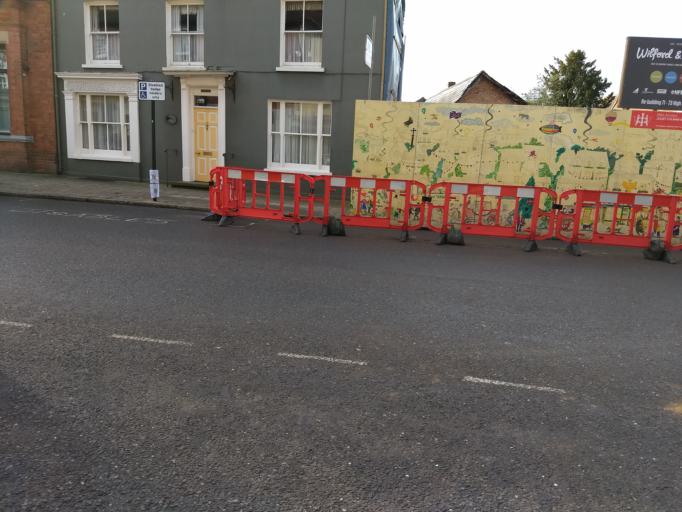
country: GB
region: England
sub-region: Milton Keynes
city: Stony Stratford
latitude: 52.0577
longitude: -0.8541
